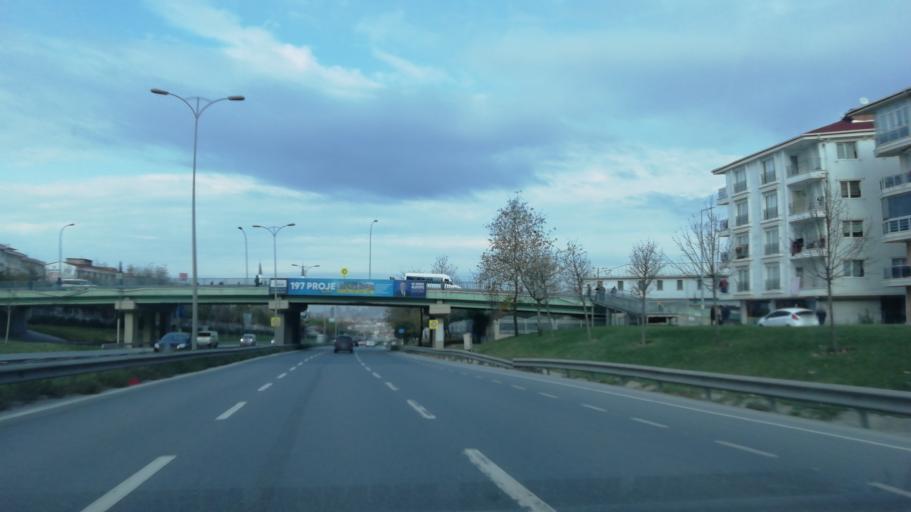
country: TR
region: Istanbul
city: Esenyurt
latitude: 41.0327
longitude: 28.6869
